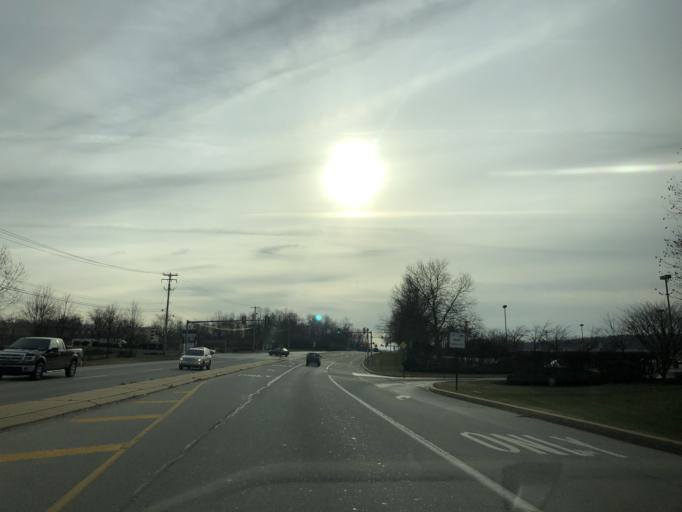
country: US
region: Pennsylvania
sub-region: Chester County
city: Downingtown
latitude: 40.0179
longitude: -75.6750
